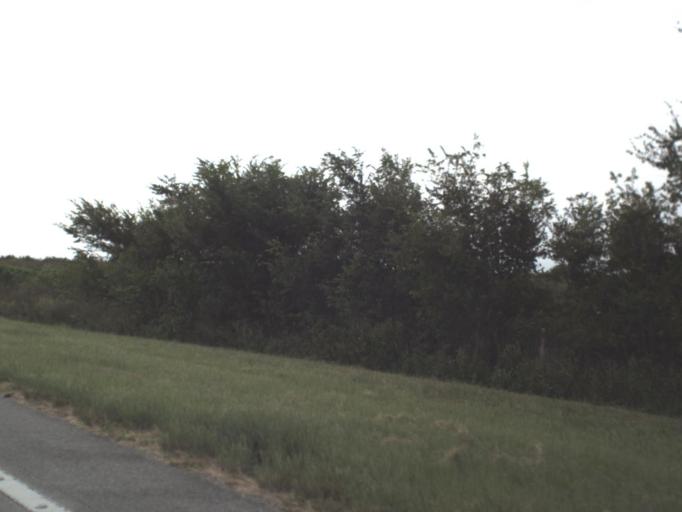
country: US
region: Florida
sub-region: Hendry County
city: Port LaBelle
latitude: 26.7684
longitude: -81.2747
